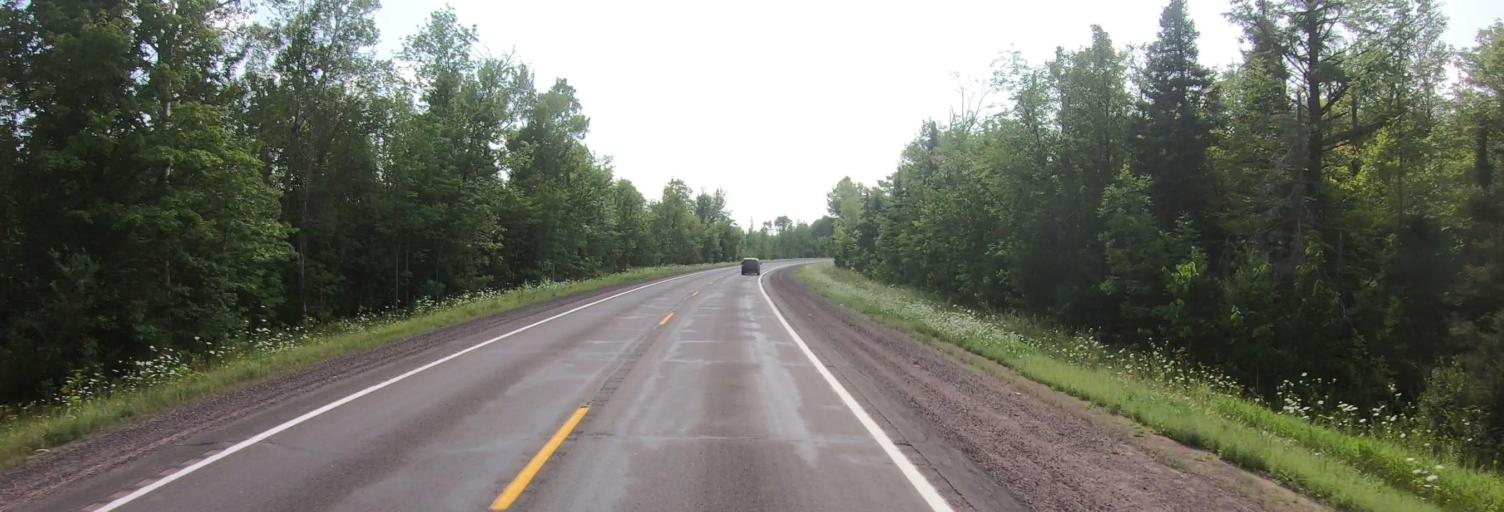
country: US
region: Michigan
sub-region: Ontonagon County
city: Ontonagon
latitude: 46.7375
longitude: -89.1125
